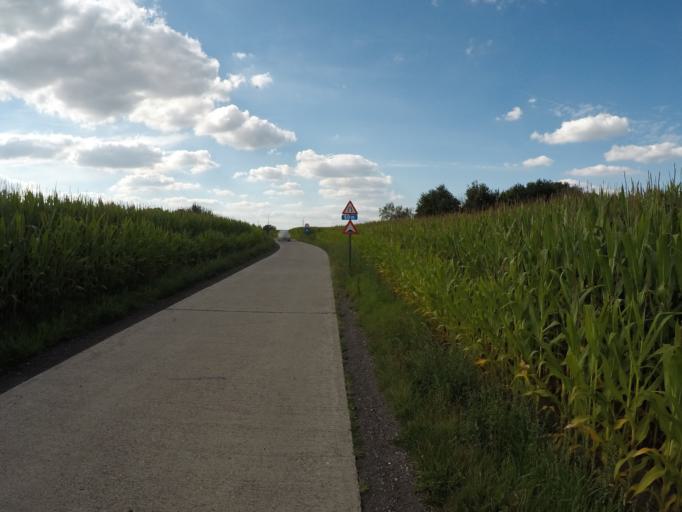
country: BE
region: Flanders
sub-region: Provincie Antwerpen
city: Ranst
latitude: 51.1707
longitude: 4.6102
